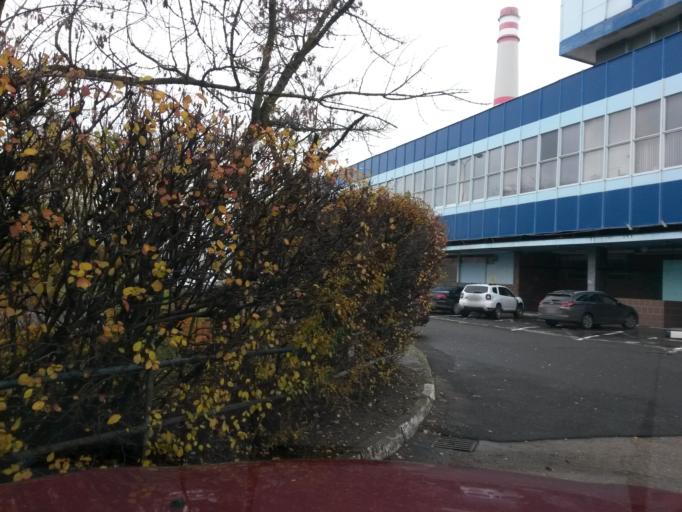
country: SK
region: Kosicky
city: Cierna nad Tisou
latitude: 48.5546
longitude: 21.9735
